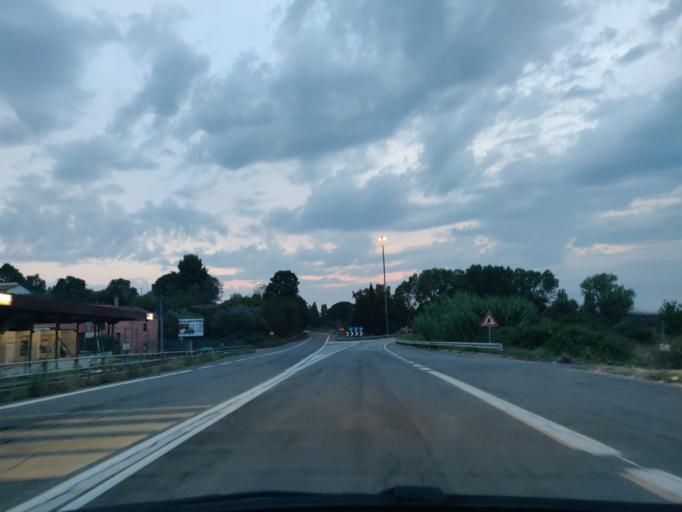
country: IT
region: Latium
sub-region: Provincia di Viterbo
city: Vetralla
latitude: 42.3719
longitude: 12.0608
